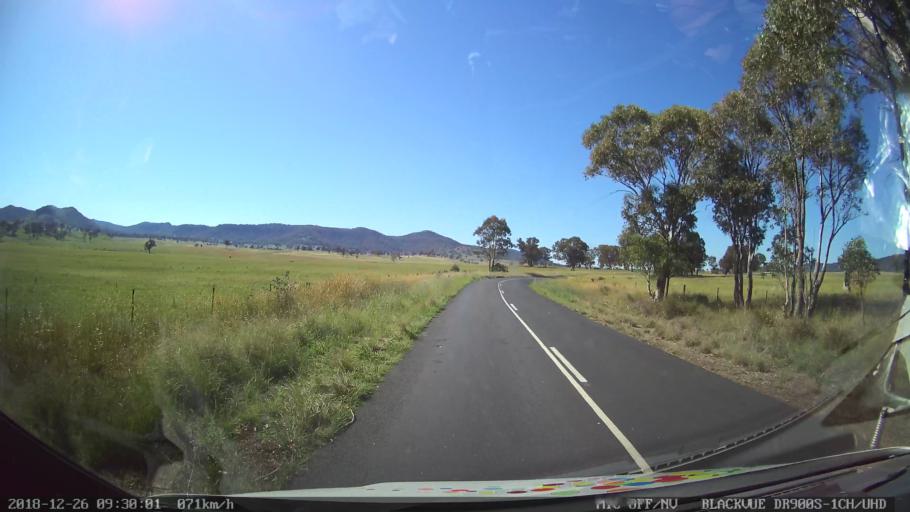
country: AU
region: New South Wales
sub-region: Mid-Western Regional
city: Kandos
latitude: -32.8589
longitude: 150.0302
